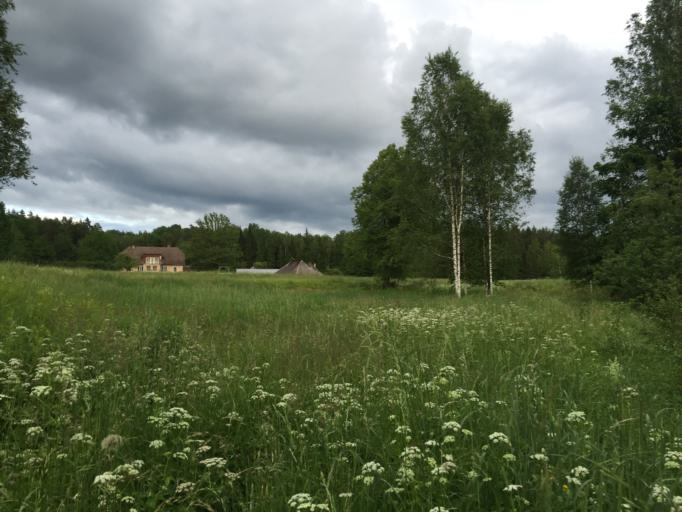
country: LV
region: Ligatne
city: Ligatne
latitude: 57.2392
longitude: 25.1516
